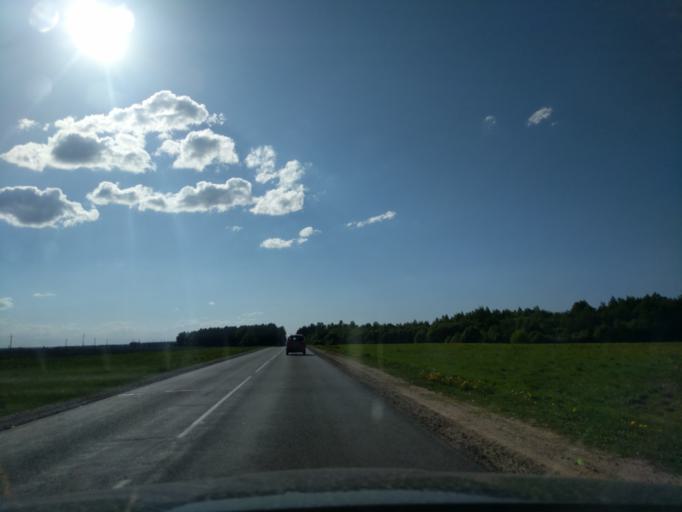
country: BY
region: Vitebsk
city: Pastavy
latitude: 55.1115
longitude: 26.8987
